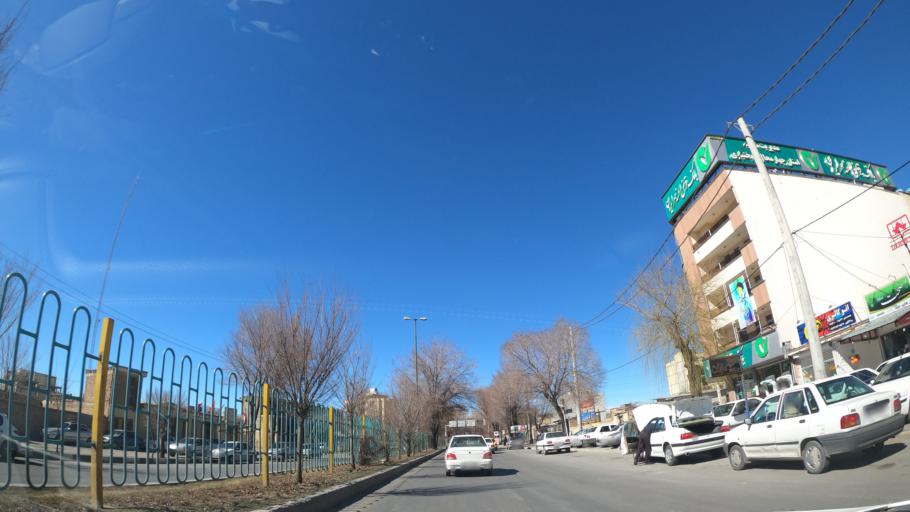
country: IR
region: Chahar Mahall va Bakhtiari
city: Shahrekord
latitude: 32.3109
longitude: 50.8875
